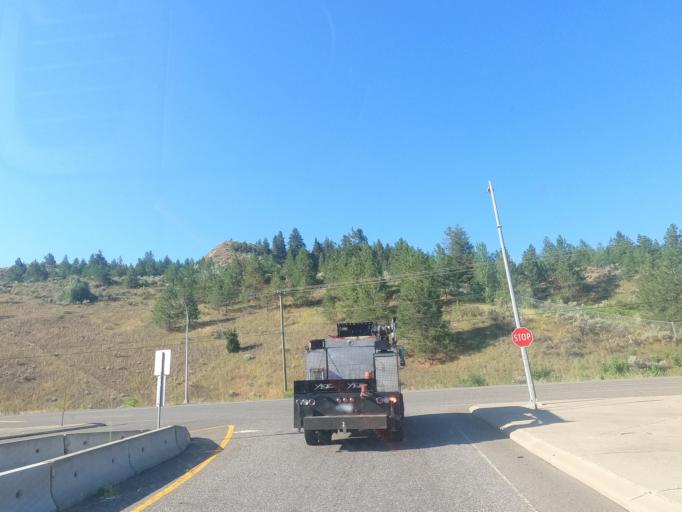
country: CA
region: British Columbia
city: Kamloops
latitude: 50.6535
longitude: -120.0709
